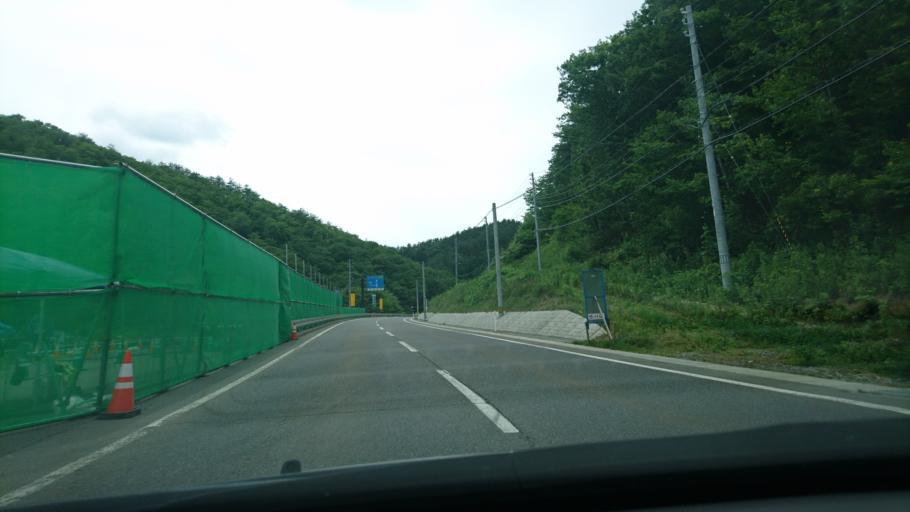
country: JP
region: Iwate
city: Miyako
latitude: 39.9280
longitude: 141.8828
